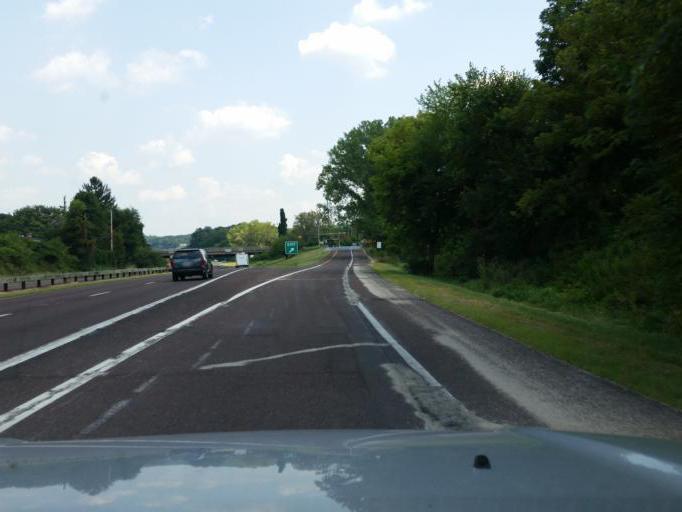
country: US
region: Pennsylvania
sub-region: Dauphin County
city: Hummelstown
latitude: 40.2586
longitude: -76.7127
